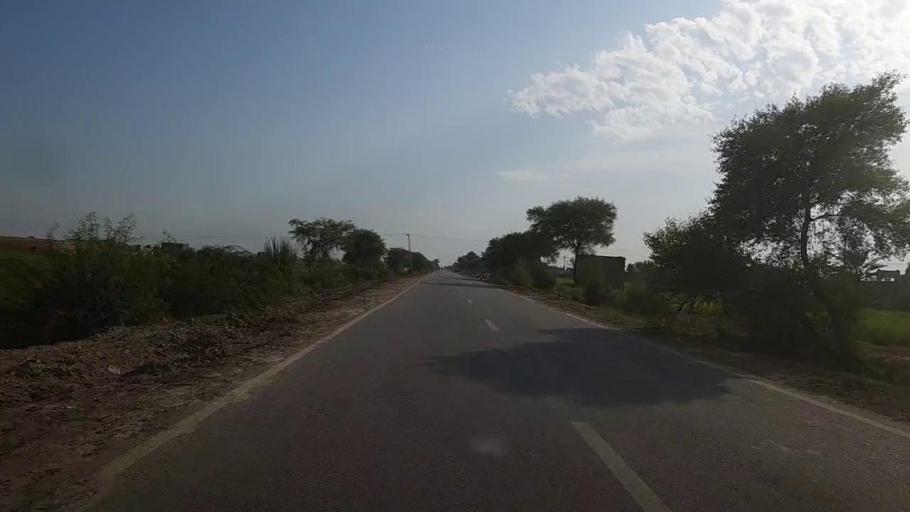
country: PK
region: Sindh
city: Thul
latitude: 28.2204
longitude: 68.7579
